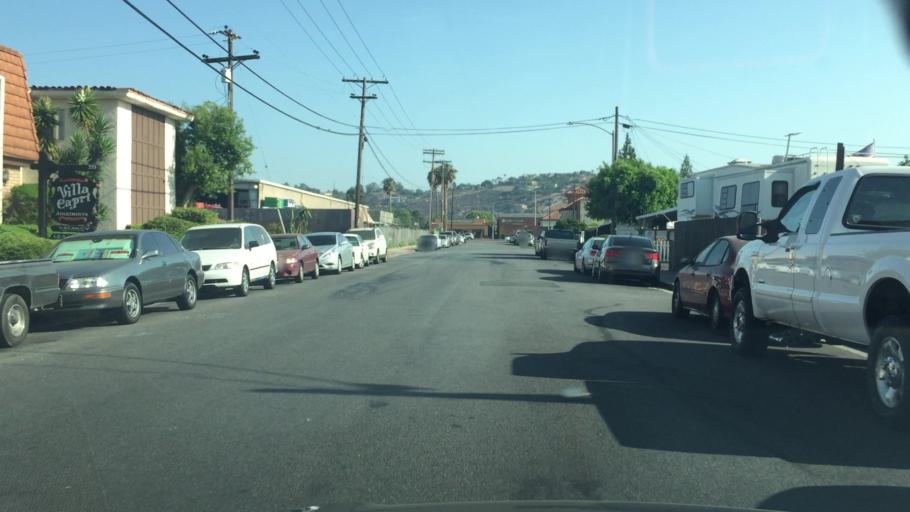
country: US
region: California
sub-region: San Diego County
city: Bostonia
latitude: 32.7969
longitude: -116.9380
